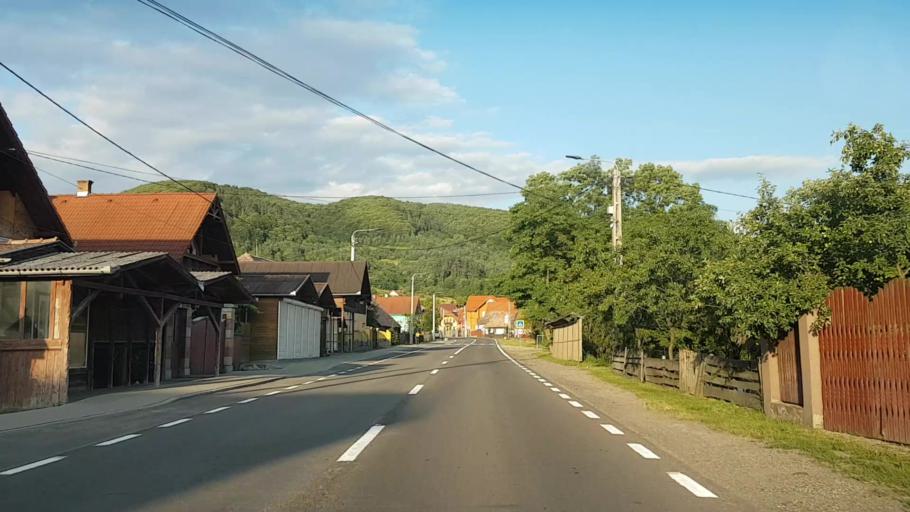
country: RO
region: Harghita
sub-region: Comuna Corund
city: Corund
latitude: 46.4699
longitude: 25.1932
